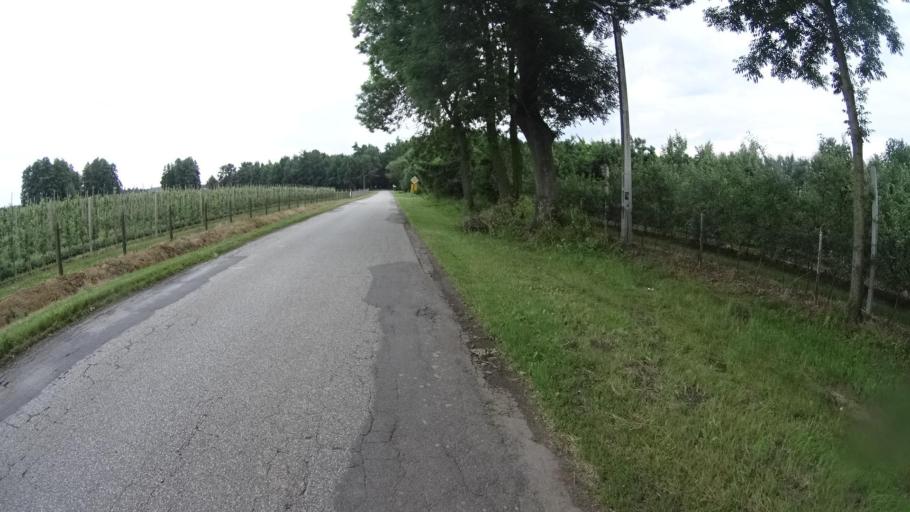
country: PL
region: Masovian Voivodeship
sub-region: Powiat grojecki
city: Goszczyn
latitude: 51.7841
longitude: 20.8547
